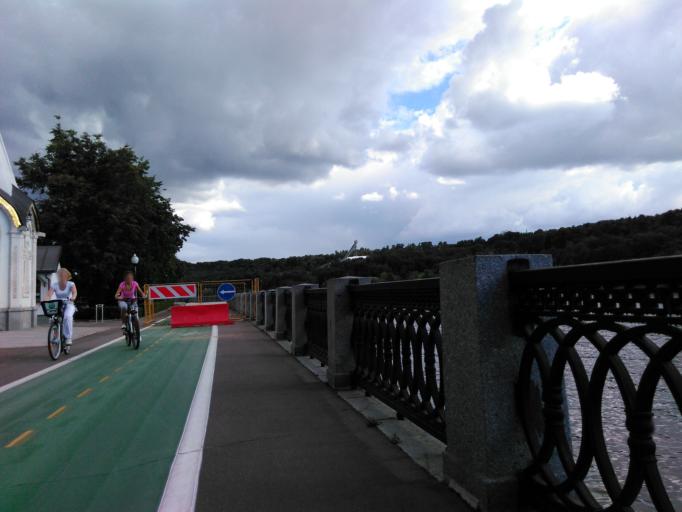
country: RU
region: Moscow
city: Vorob'yovo
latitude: 55.7183
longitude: 37.5432
